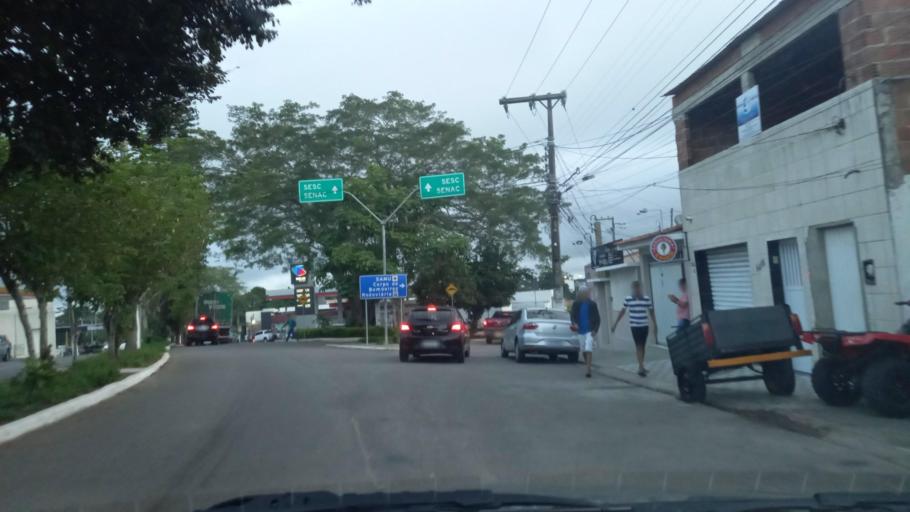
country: BR
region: Pernambuco
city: Garanhuns
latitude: -8.8793
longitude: -36.4763
